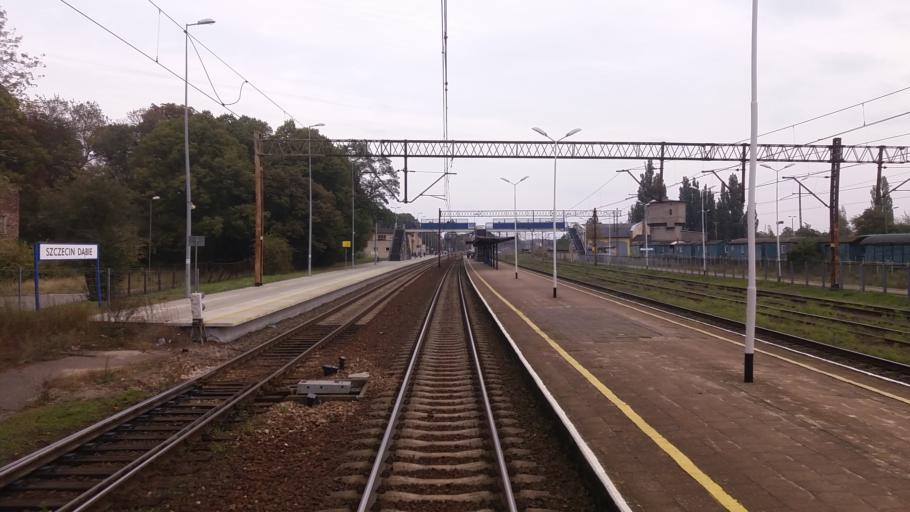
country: PL
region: West Pomeranian Voivodeship
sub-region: Szczecin
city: Szczecin
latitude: 53.3910
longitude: 14.6674
